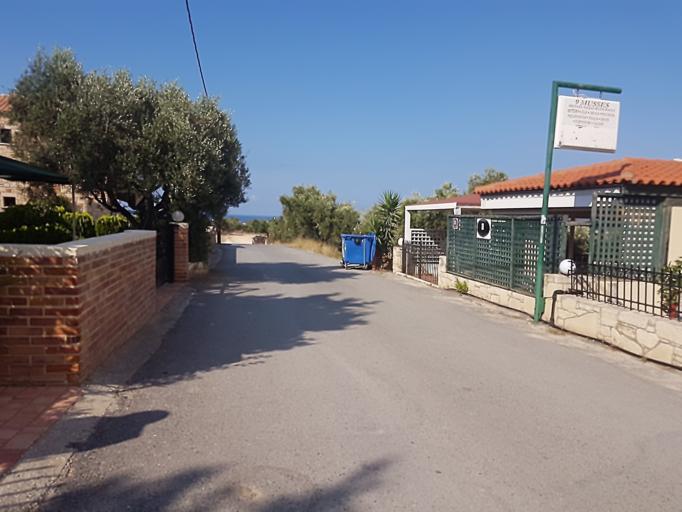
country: GR
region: Crete
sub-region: Nomos Irakleiou
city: Limin Khersonisou
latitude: 35.3161
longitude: 25.3867
